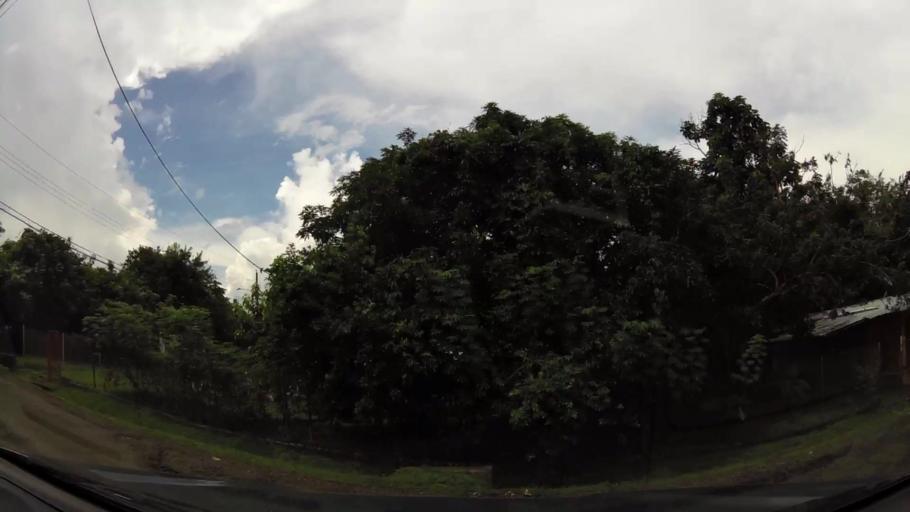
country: PA
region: Panama
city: Cabra Numero Uno
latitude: 9.1072
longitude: -79.3238
